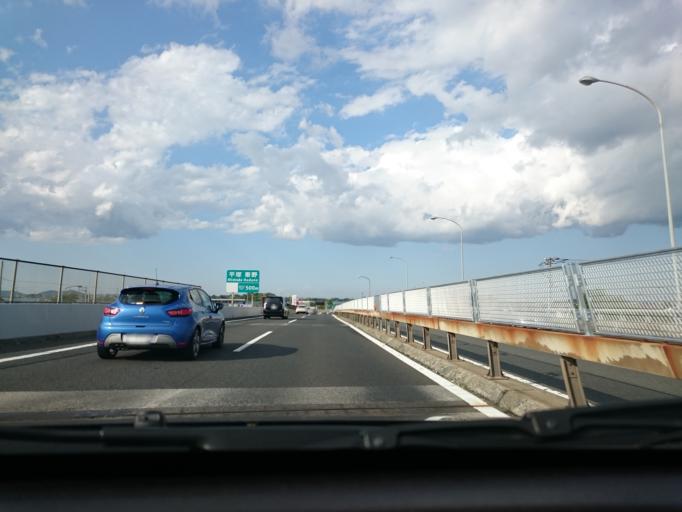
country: JP
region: Kanagawa
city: Isehara
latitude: 35.3584
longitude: 139.3024
